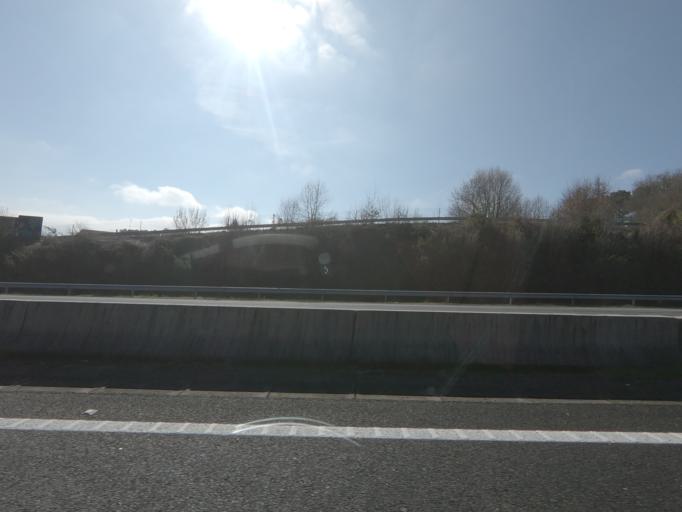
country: ES
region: Galicia
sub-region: Provincia de Ourense
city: Maside
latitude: 42.3999
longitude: -8.0039
